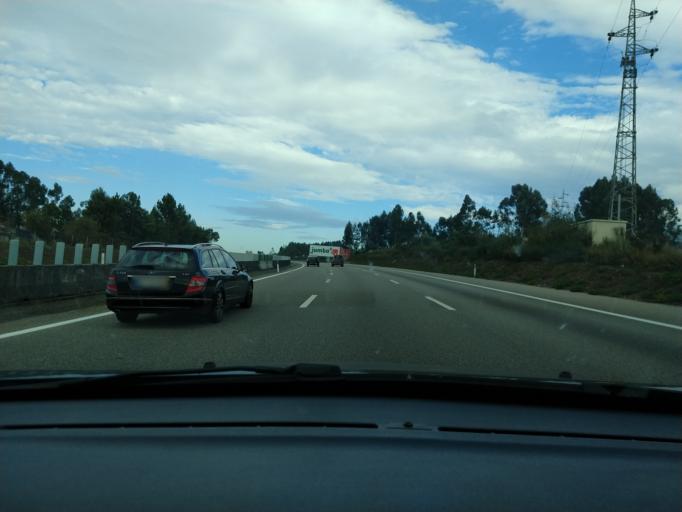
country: PT
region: Aveiro
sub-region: Santa Maria da Feira
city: Rio Meao
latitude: 40.9651
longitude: -8.5677
